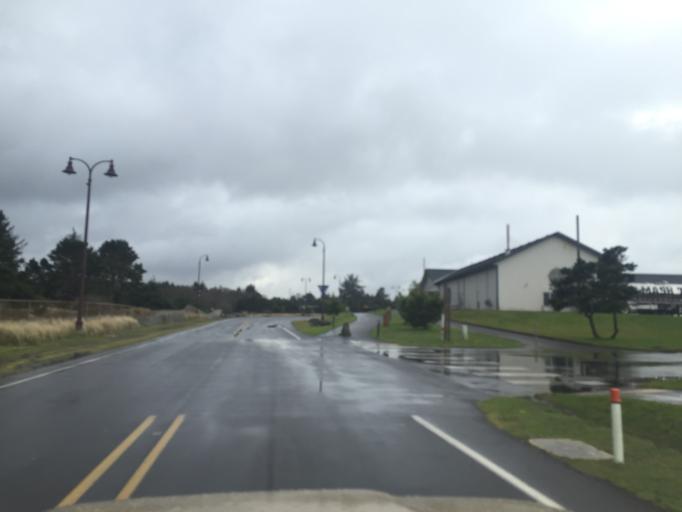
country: US
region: Oregon
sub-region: Lincoln County
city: Newport
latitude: 44.6211
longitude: -124.0475
